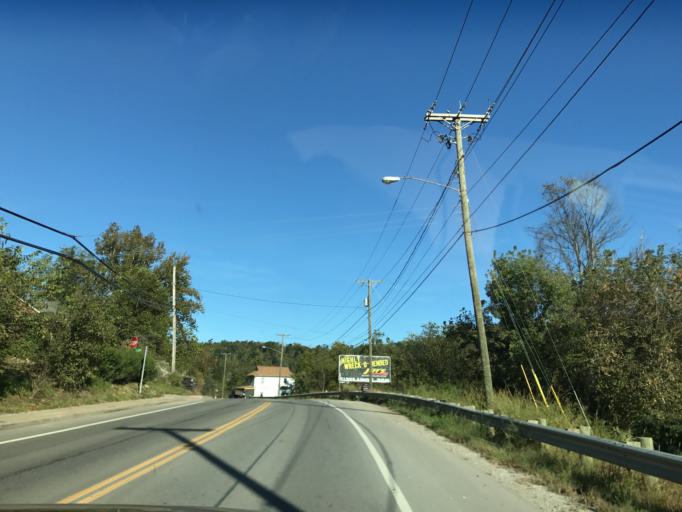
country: US
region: Ohio
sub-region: Belmont County
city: Wolfhurst
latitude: 40.0670
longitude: -80.8069
